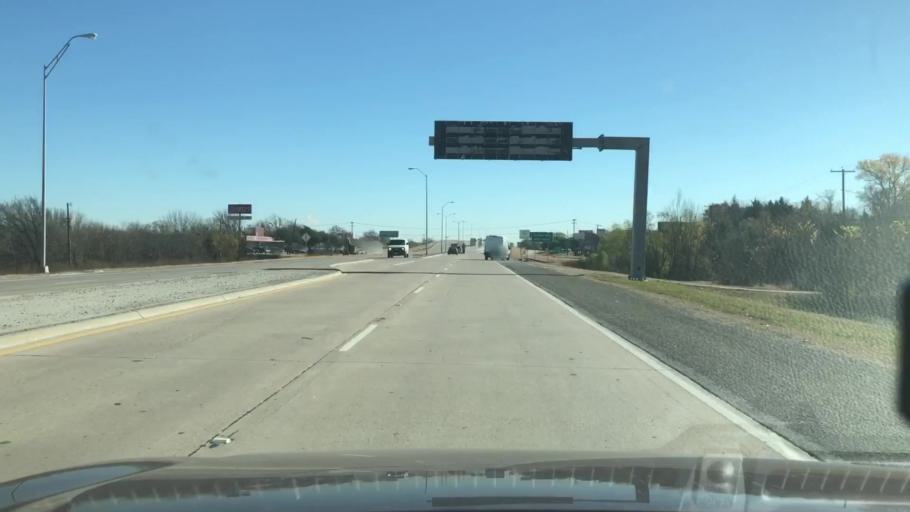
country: US
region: Texas
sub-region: Dallas County
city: Farmers Branch
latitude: 32.8718
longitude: -96.9236
